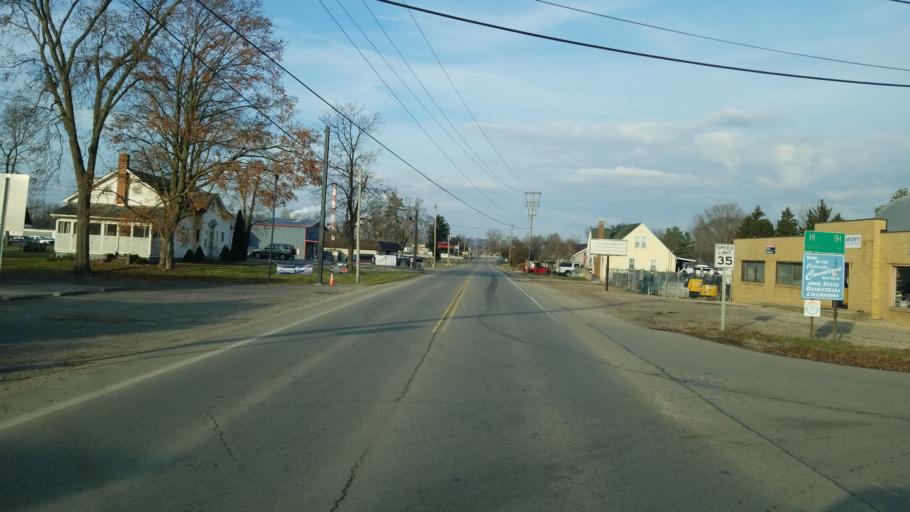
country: US
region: Ohio
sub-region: Ross County
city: Chillicothe
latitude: 39.3231
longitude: -82.9555
